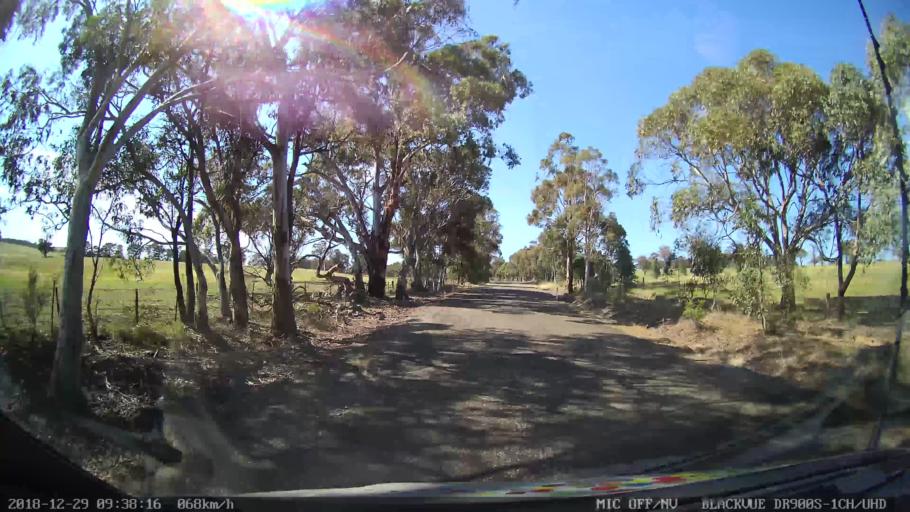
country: AU
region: New South Wales
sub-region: Upper Lachlan Shire
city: Crookwell
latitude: -34.6452
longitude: 149.3761
